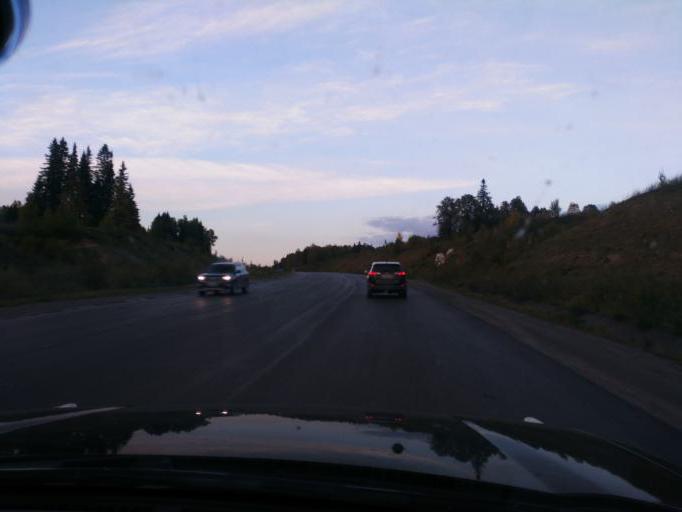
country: RU
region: Perm
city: Polazna
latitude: 58.2870
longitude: 56.4757
